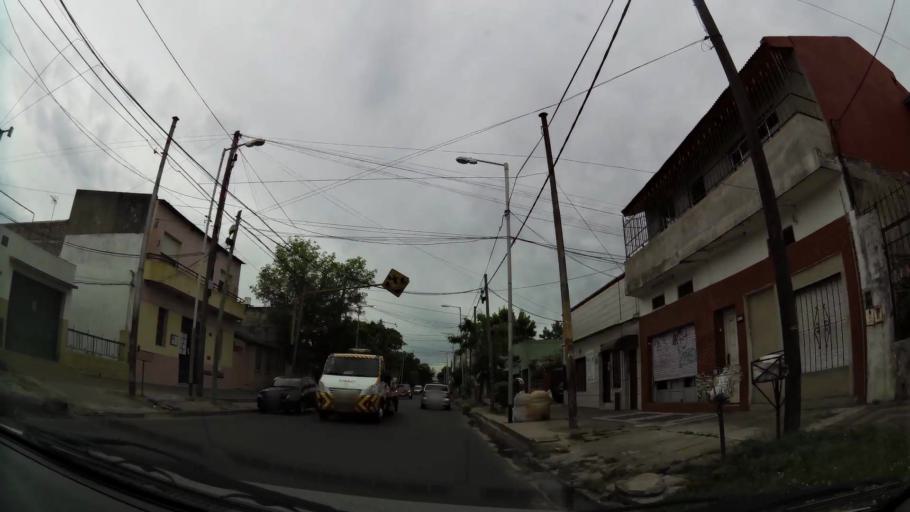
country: AR
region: Buenos Aires
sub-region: Partido de Lanus
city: Lanus
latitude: -34.6924
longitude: -58.3711
